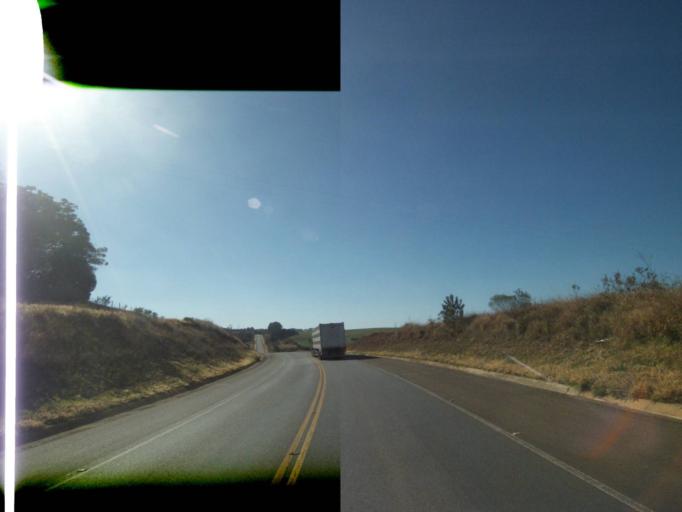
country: BR
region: Parana
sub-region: Tibagi
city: Tibagi
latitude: -24.5399
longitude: -50.4468
